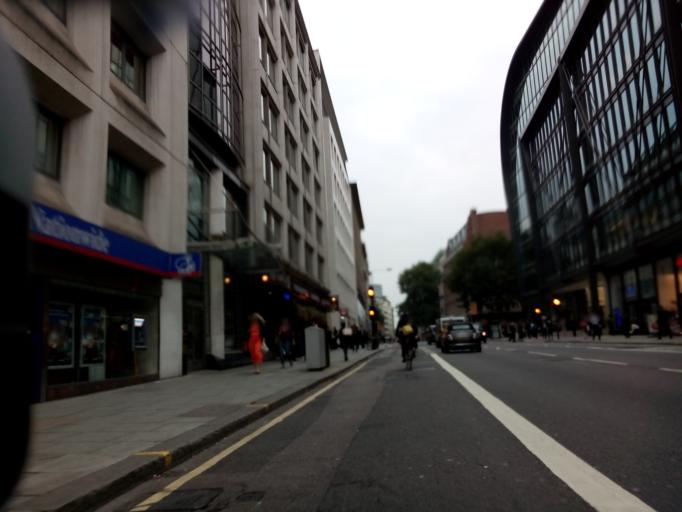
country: GB
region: England
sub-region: Greater London
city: Clerkenwell
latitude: 51.5181
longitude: -0.1149
